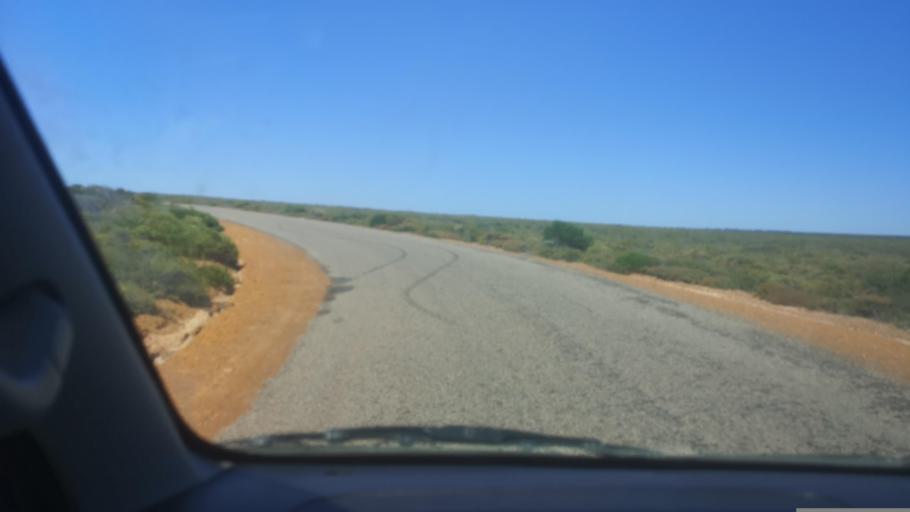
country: AU
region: Western Australia
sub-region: Northampton Shire
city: Kalbarri
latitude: -27.8274
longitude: 114.1158
